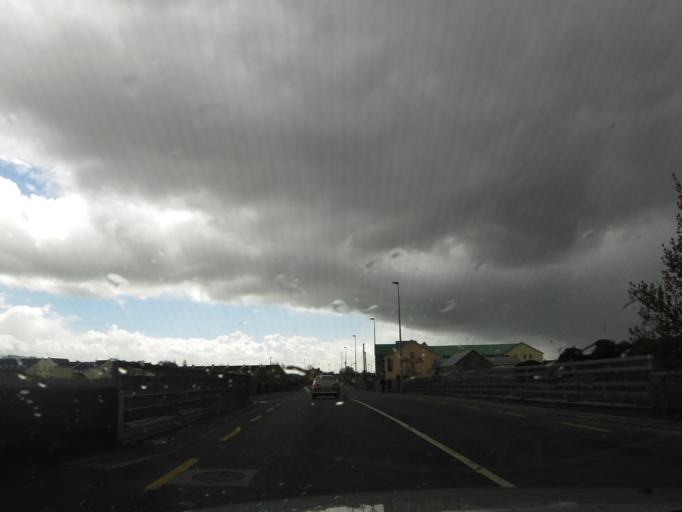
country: IE
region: Connaught
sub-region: County Galway
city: Claregalway
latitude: 53.3461
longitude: -8.9423
